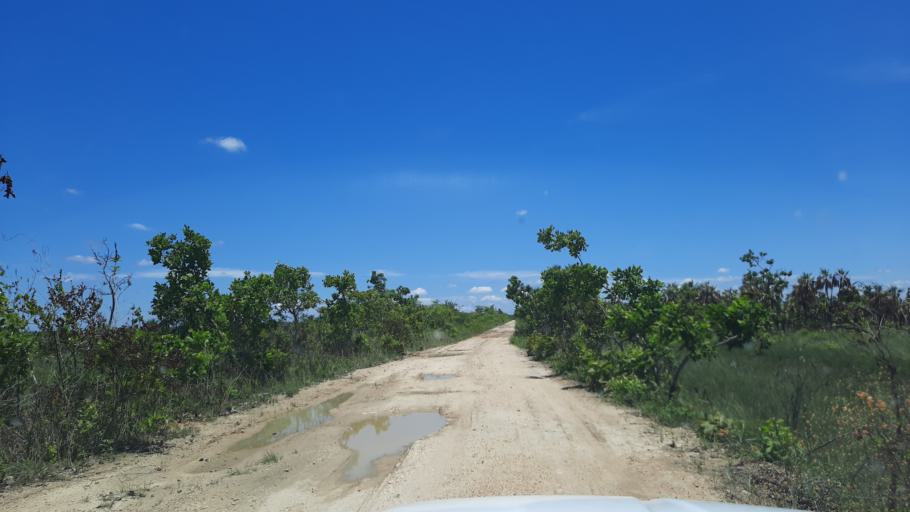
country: BZ
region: Cayo
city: Belmopan
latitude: 17.3788
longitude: -88.4899
